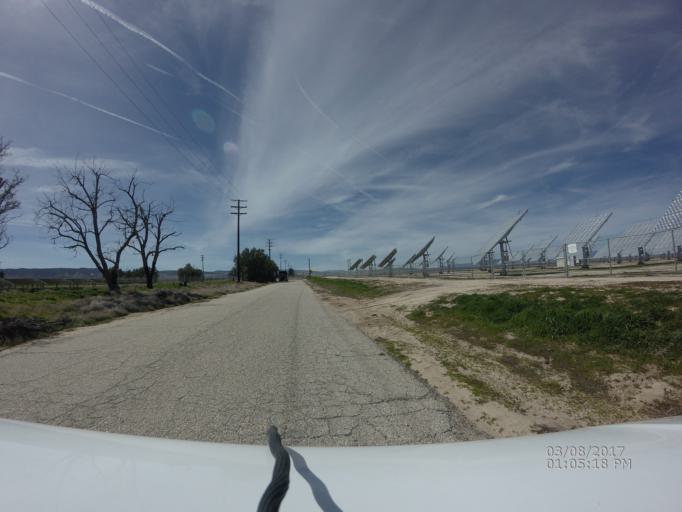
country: US
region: California
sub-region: Los Angeles County
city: Leona Valley
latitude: 34.7185
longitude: -118.2925
